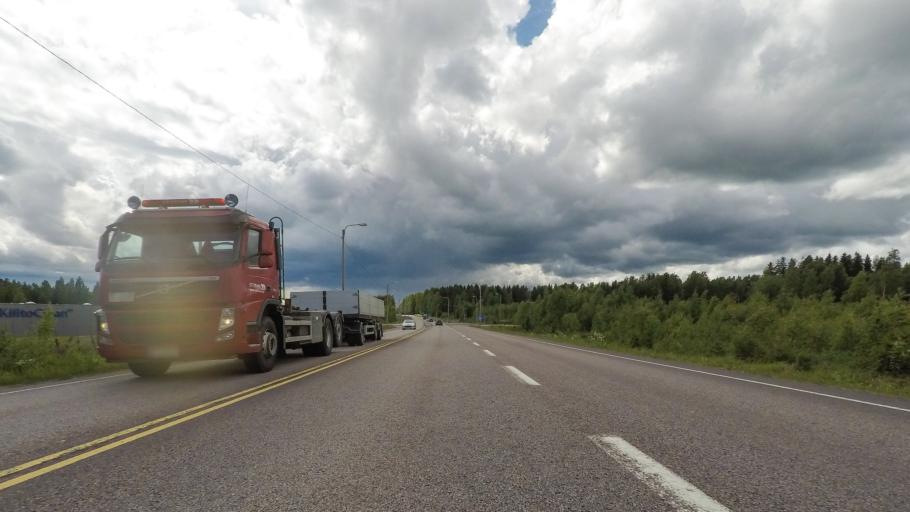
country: FI
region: Central Finland
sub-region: Jyvaeskylae
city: Hankasalmi
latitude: 62.2862
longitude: 26.3501
